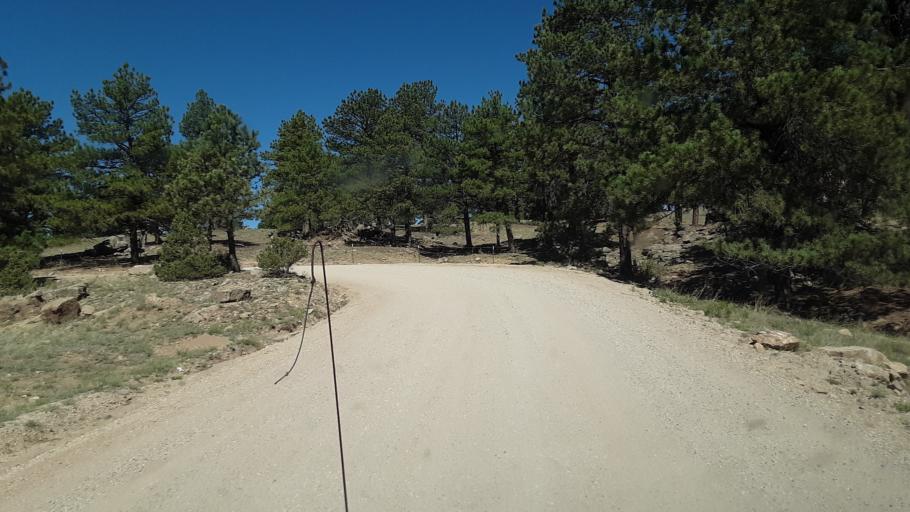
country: US
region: Colorado
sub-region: Custer County
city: Westcliffe
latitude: 38.2126
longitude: -105.4431
